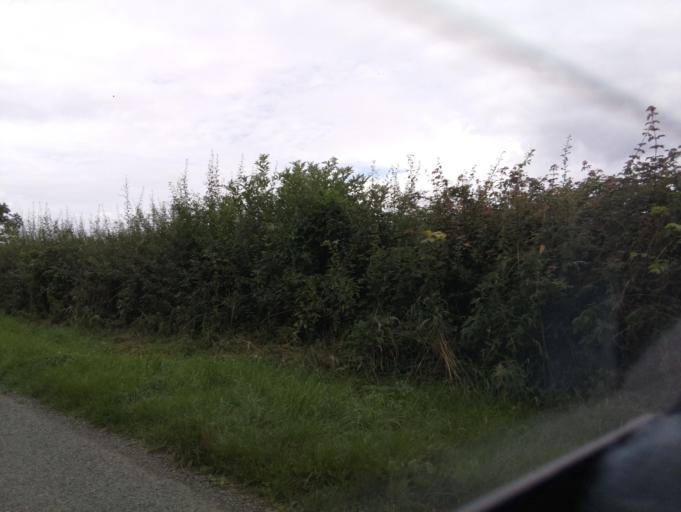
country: GB
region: England
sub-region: Northamptonshire
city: Corby
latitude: 52.5203
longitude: -0.6337
